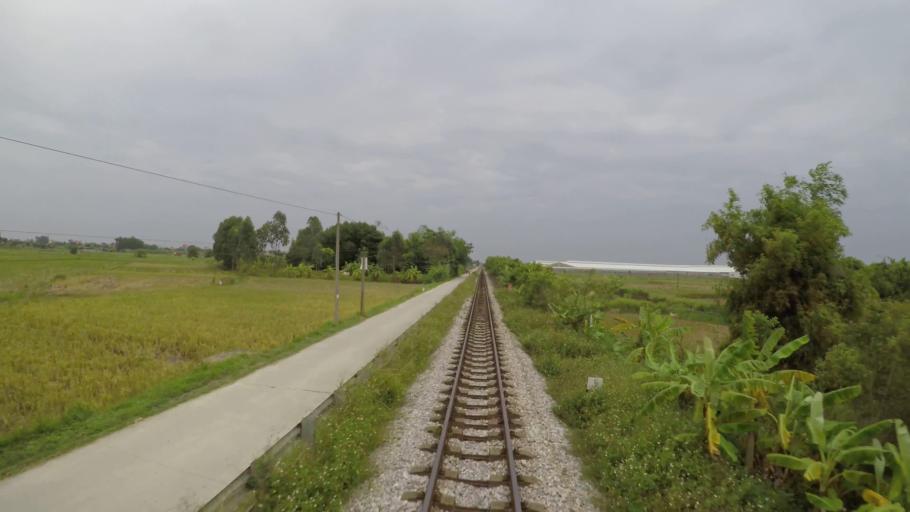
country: VN
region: Hai Duong
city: Lai Cach
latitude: 20.9526
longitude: 106.2304
